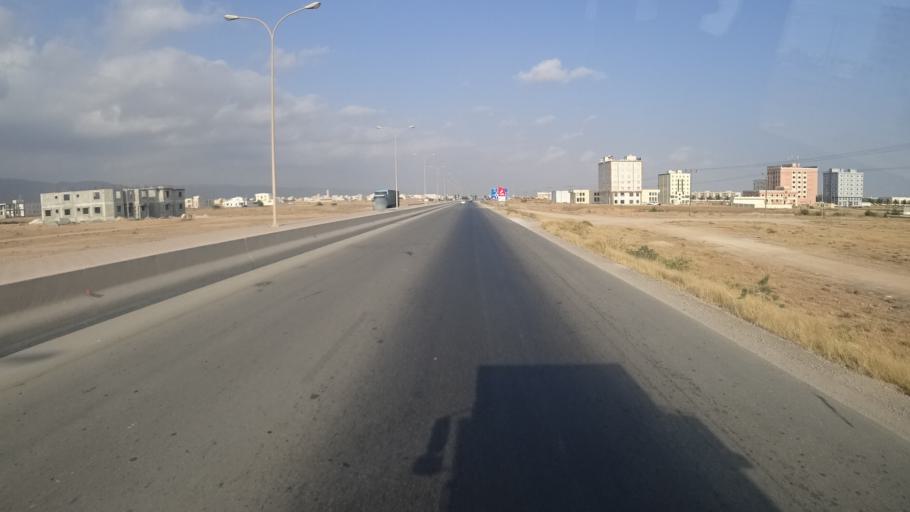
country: OM
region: Zufar
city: Salalah
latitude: 17.0280
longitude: 54.0247
